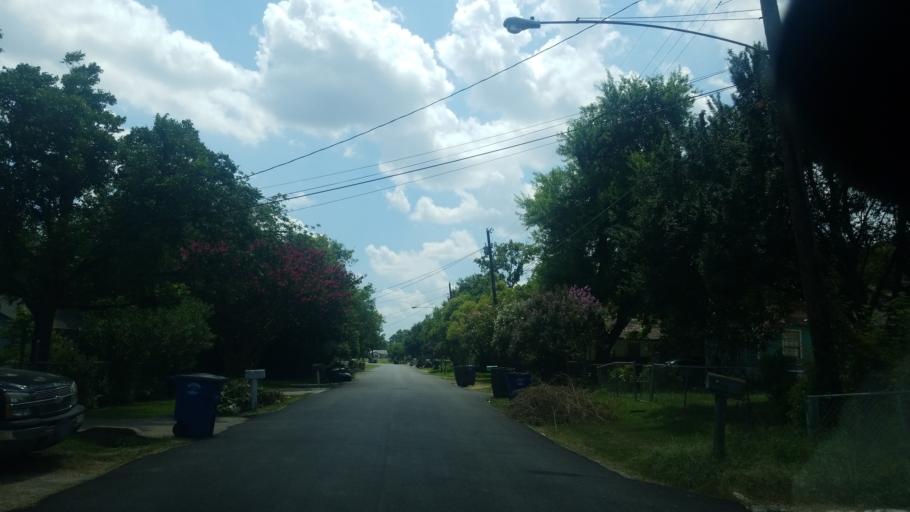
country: US
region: Texas
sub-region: Dallas County
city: Dallas
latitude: 32.7175
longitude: -96.7687
